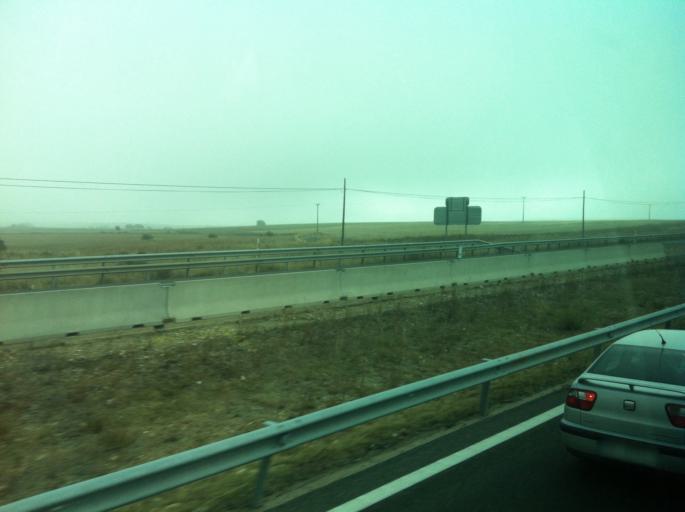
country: ES
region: Castille and Leon
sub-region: Provincia de Burgos
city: Saldana de Burgos
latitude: 42.2382
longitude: -3.7059
